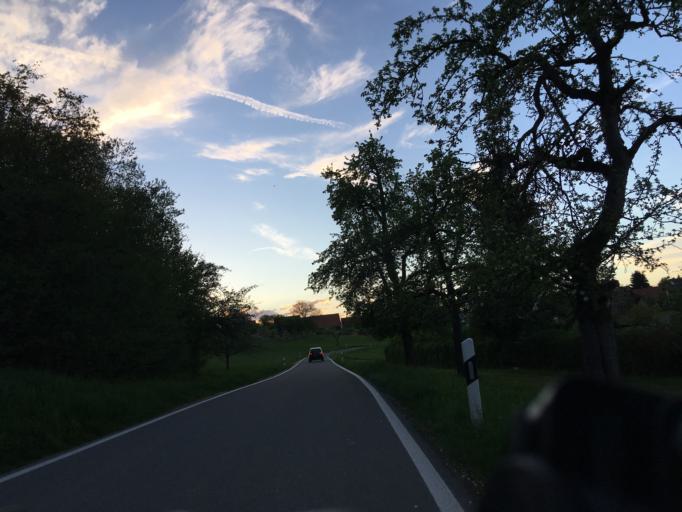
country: DE
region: Baden-Wuerttemberg
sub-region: Freiburg Region
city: Gailingen
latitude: 47.7194
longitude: 8.7581
